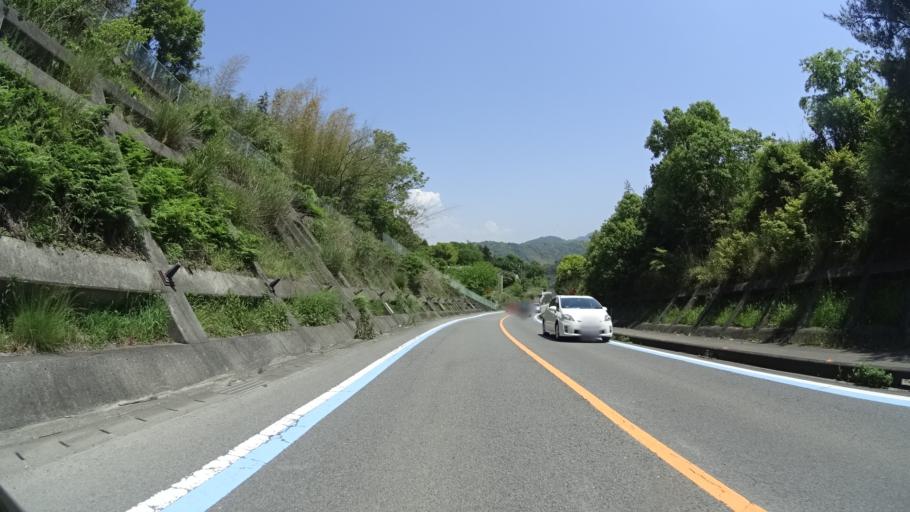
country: JP
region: Ehime
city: Iyo
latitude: 33.7272
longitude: 132.6857
